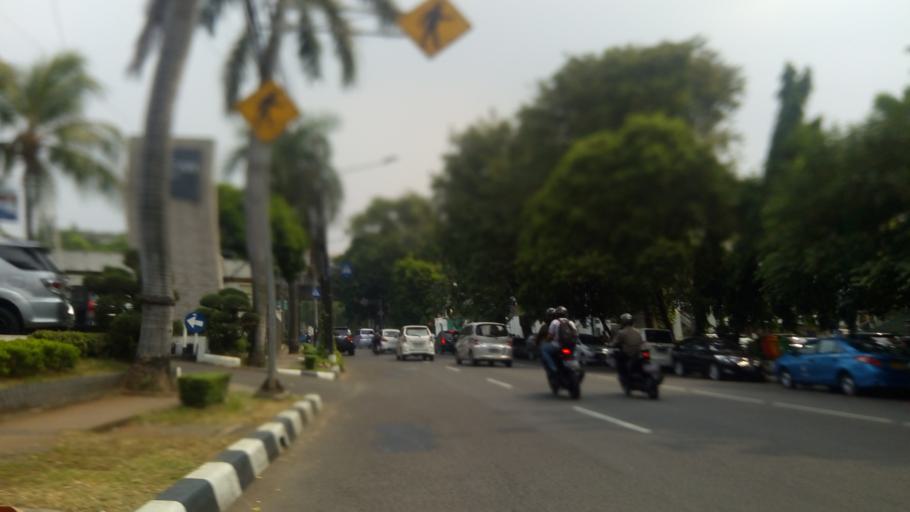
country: ID
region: Jakarta Raya
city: Jakarta
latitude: -6.1873
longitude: 106.8343
